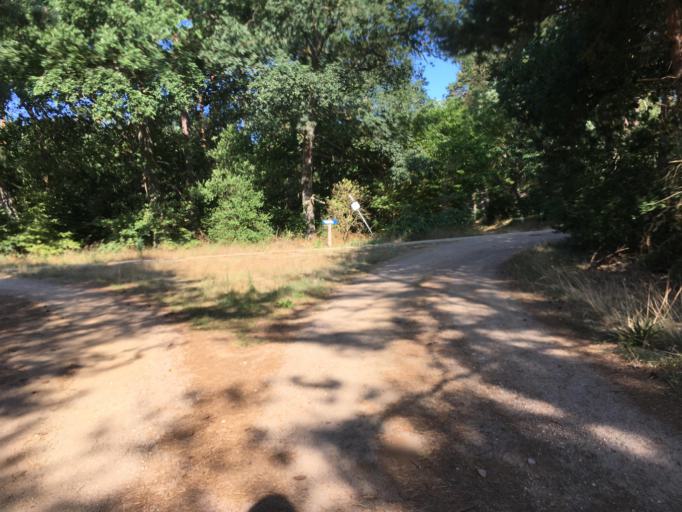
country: DE
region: Brandenburg
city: Liebenwalde
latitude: 52.9158
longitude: 13.4296
